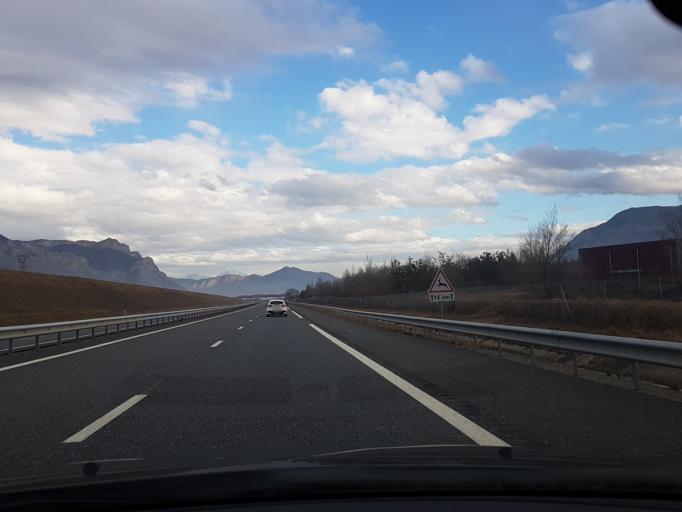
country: FR
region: Provence-Alpes-Cote d'Azur
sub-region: Departement des Hautes-Alpes
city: Laragne-Monteglin
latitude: 44.3477
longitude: 5.9094
